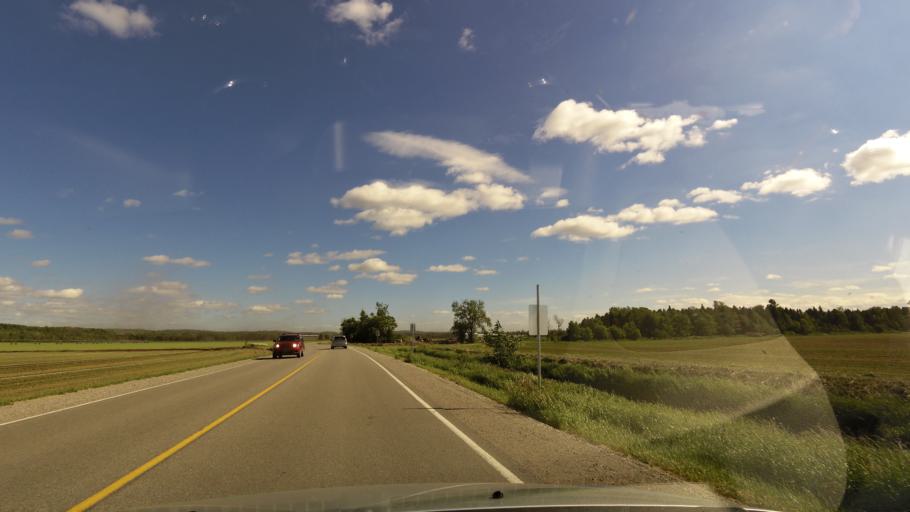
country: CA
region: Ontario
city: Innisfil
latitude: 44.2263
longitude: -79.6334
